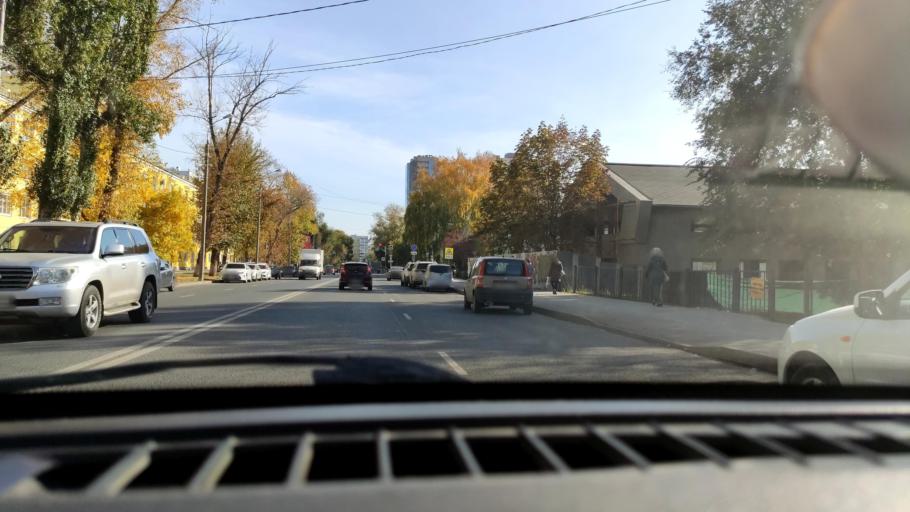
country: RU
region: Samara
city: Samara
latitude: 53.1911
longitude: 50.1269
